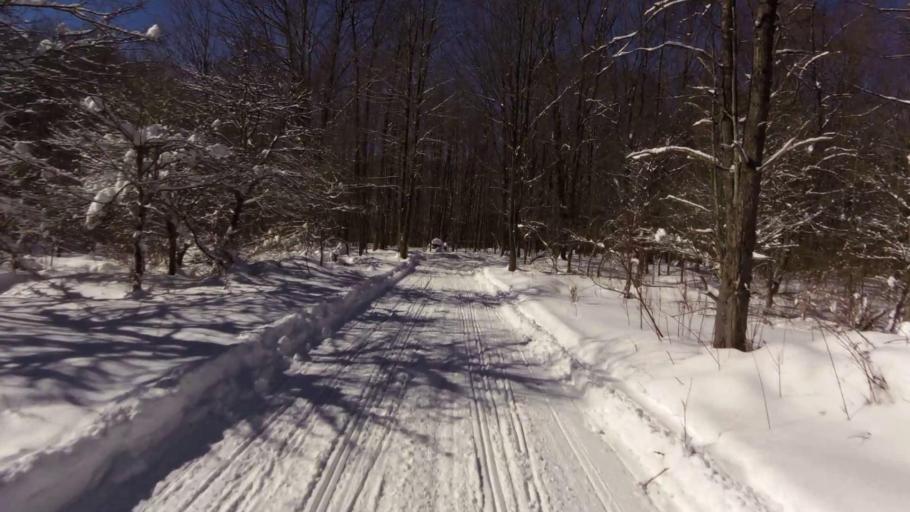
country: US
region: New York
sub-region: Chautauqua County
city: Mayville
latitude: 42.2263
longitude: -79.4053
